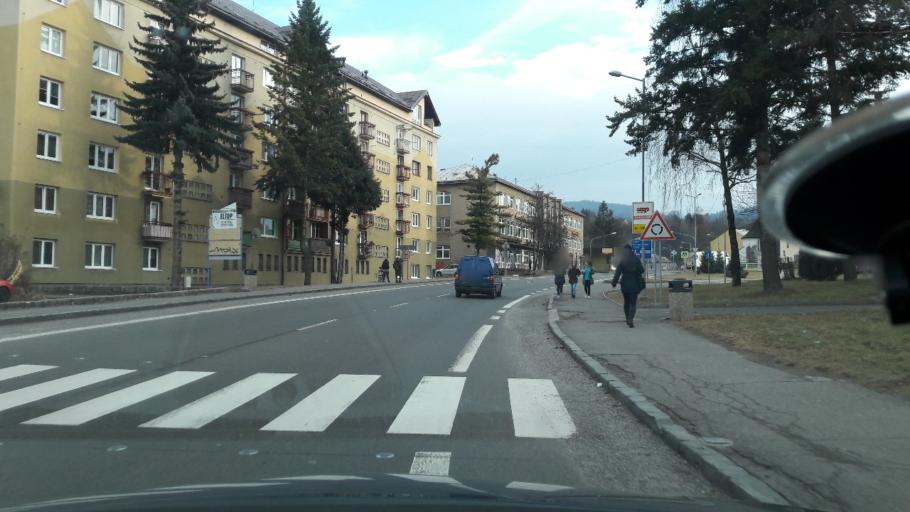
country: SK
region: Nitriansky
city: Handlova
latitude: 48.7308
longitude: 18.7606
